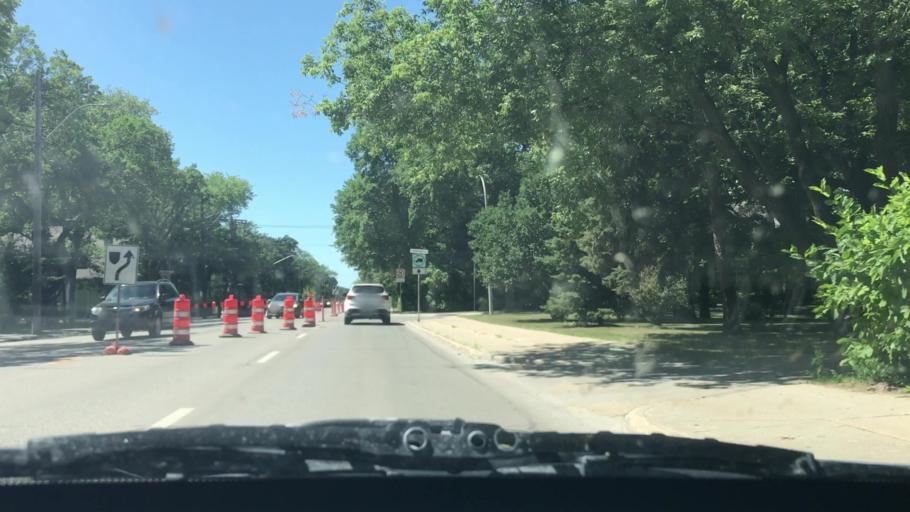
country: CA
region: Manitoba
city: Winnipeg
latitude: 49.8735
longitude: -97.1734
